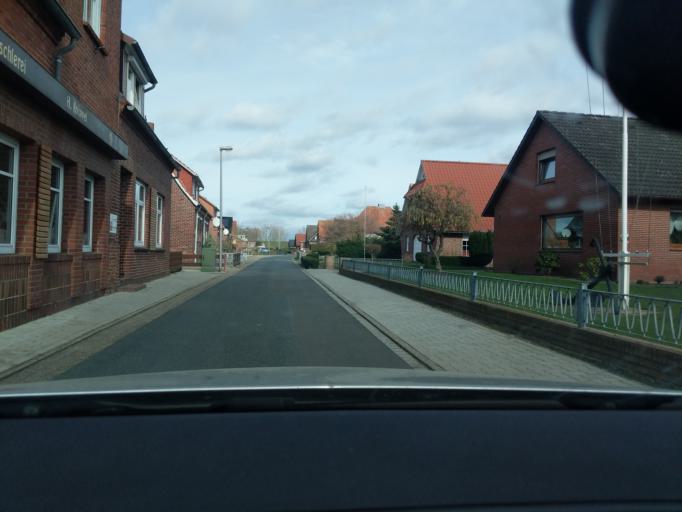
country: DE
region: Lower Saxony
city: Drochtersen
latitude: 53.7137
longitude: 9.3837
